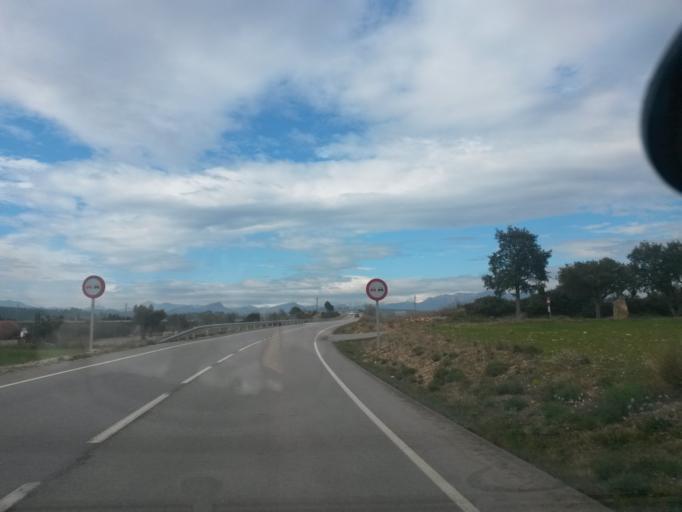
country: ES
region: Catalonia
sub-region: Provincia de Girona
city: Pont de Molins
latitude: 42.3142
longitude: 2.9496
